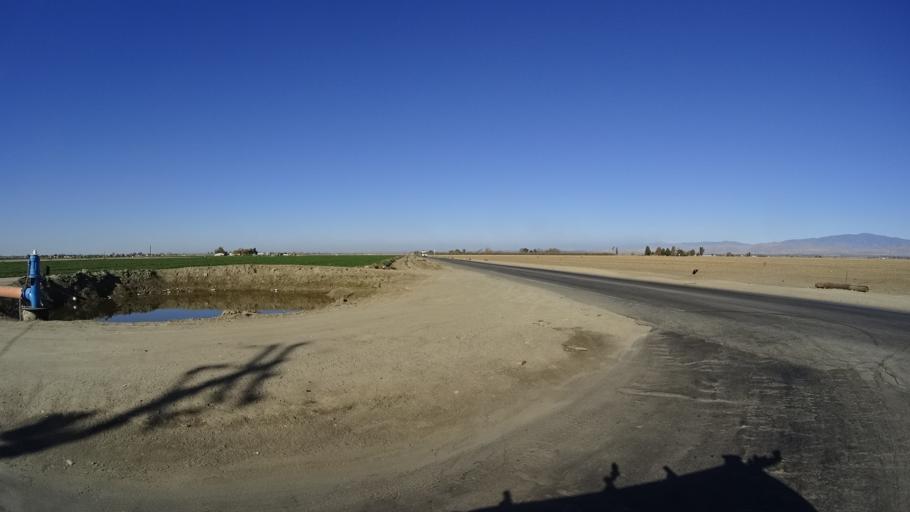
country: US
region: California
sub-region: Kern County
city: Greenfield
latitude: 35.2819
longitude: -118.9861
